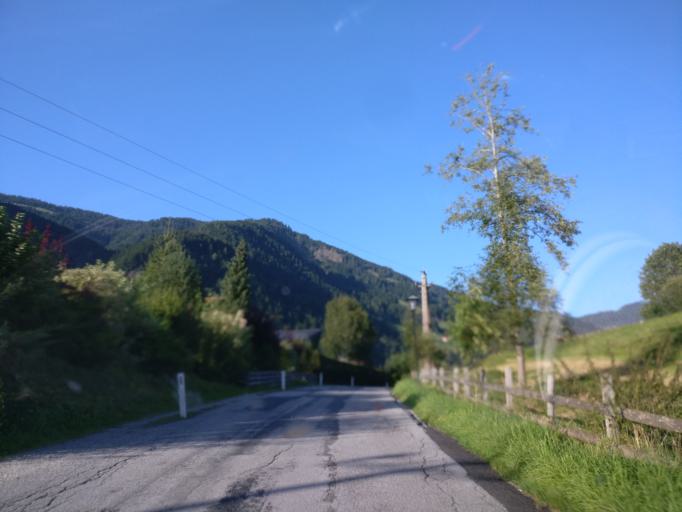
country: AT
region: Salzburg
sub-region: Politischer Bezirk Sankt Johann im Pongau
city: Goldegg
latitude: 47.3268
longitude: 13.0759
